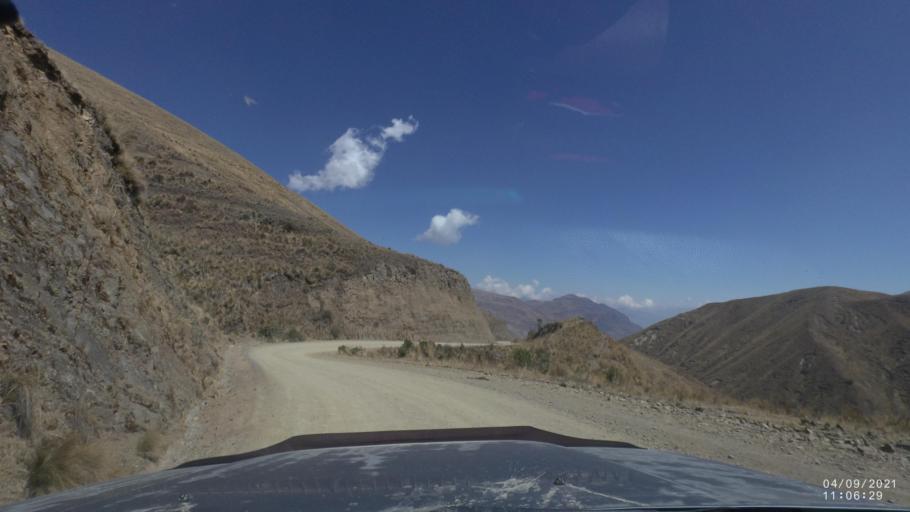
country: BO
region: Cochabamba
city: Sipe Sipe
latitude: -17.2781
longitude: -66.4705
